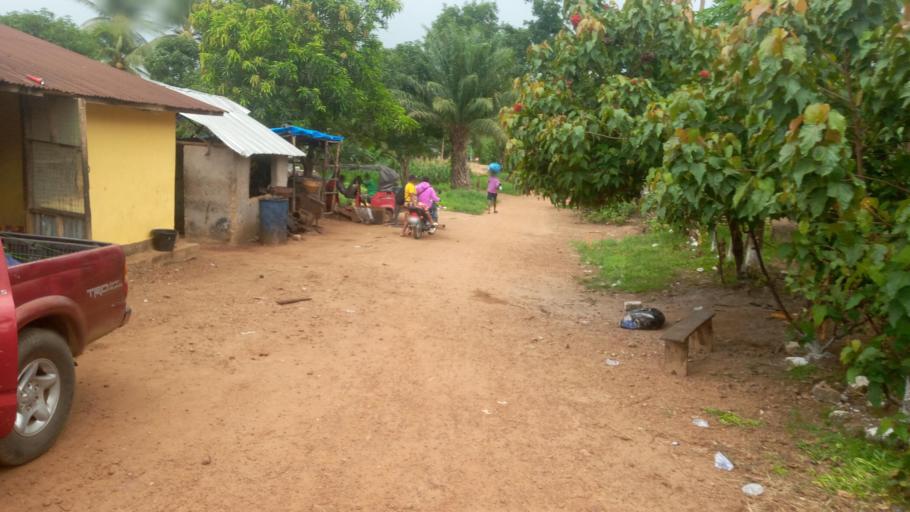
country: SL
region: Southern Province
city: Mogbwemo
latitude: 7.6052
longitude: -12.1713
